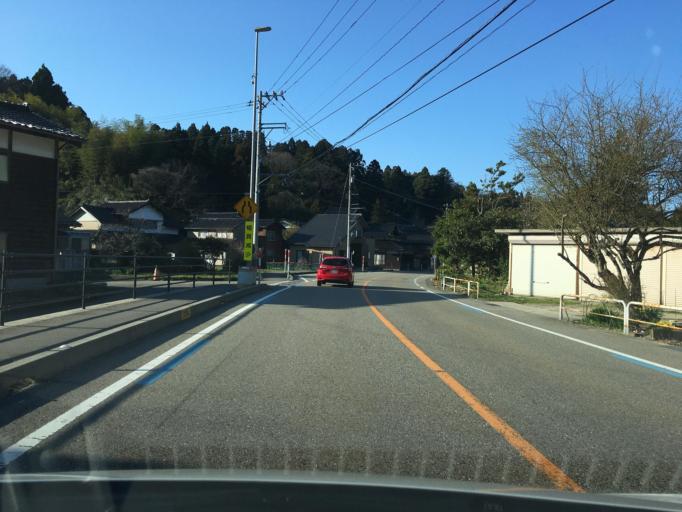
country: JP
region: Toyama
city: Himi
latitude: 36.9316
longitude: 137.0261
